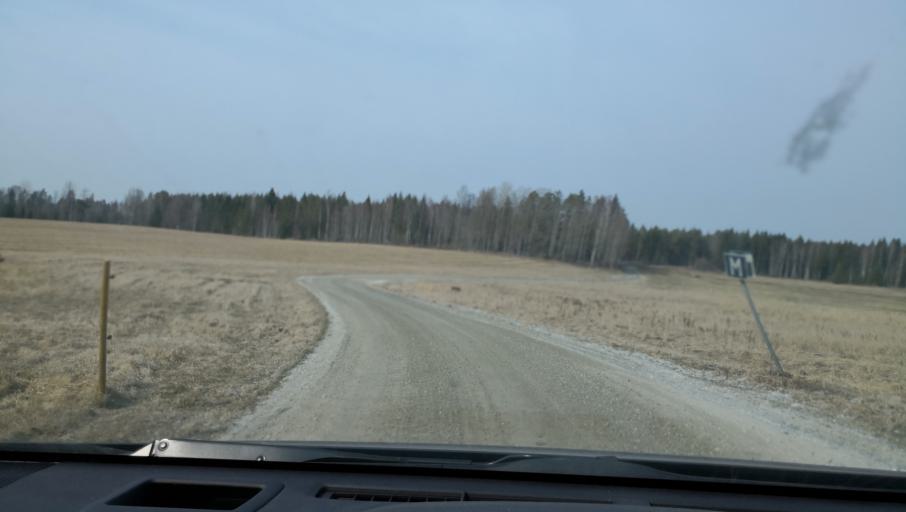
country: SE
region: OErebro
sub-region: Lindesbergs Kommun
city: Frovi
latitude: 59.3533
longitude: 15.4364
